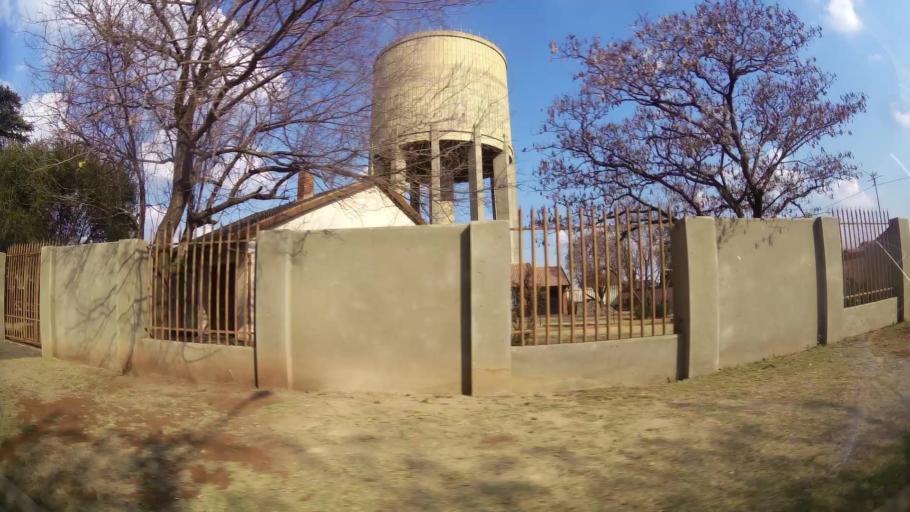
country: ZA
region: Gauteng
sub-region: Ekurhuleni Metropolitan Municipality
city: Germiston
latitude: -26.3093
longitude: 28.1912
